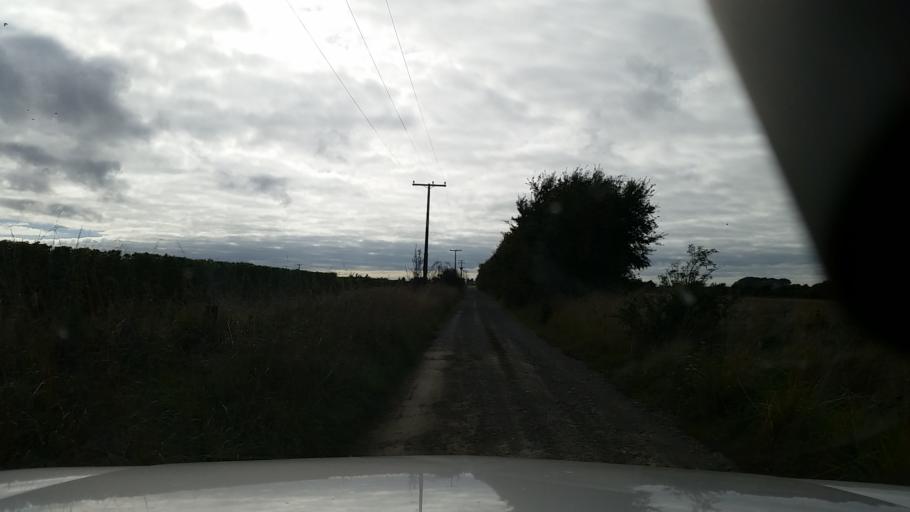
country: NZ
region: Marlborough
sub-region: Marlborough District
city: Blenheim
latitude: -41.4657
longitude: 173.9865
